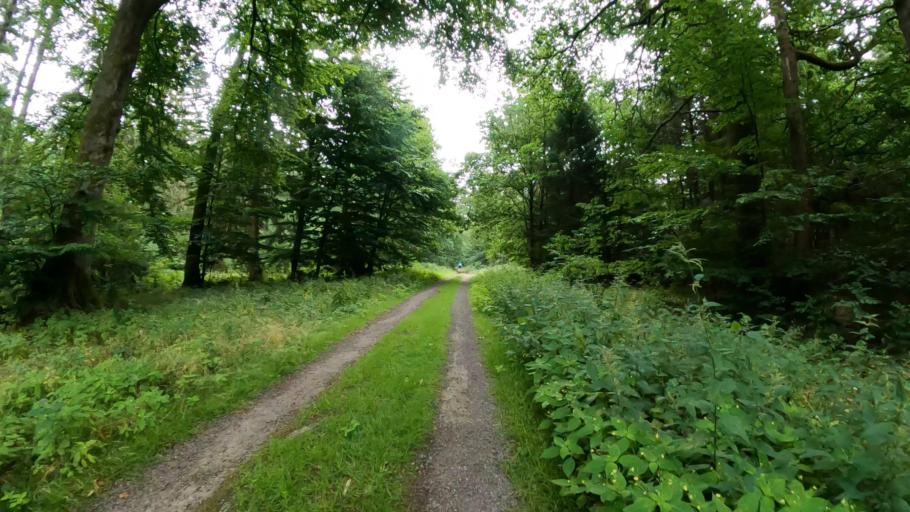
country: DE
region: Schleswig-Holstein
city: Wittenborn
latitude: 53.9303
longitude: 10.2148
